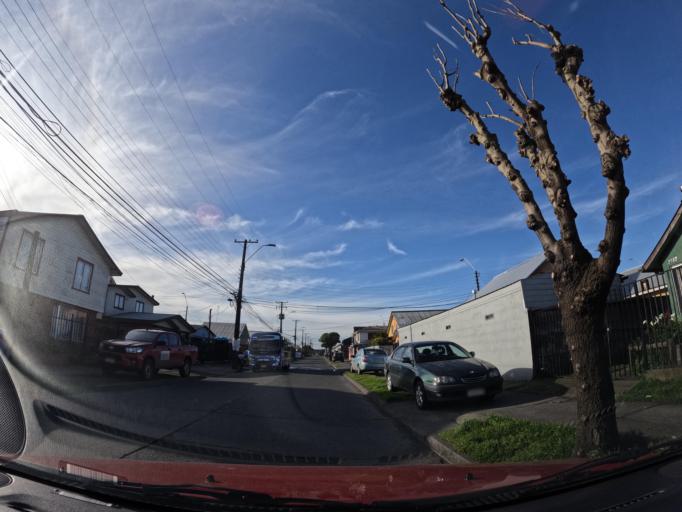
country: CL
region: Biobio
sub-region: Provincia de Concepcion
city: Talcahuano
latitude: -36.7467
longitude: -73.0861
